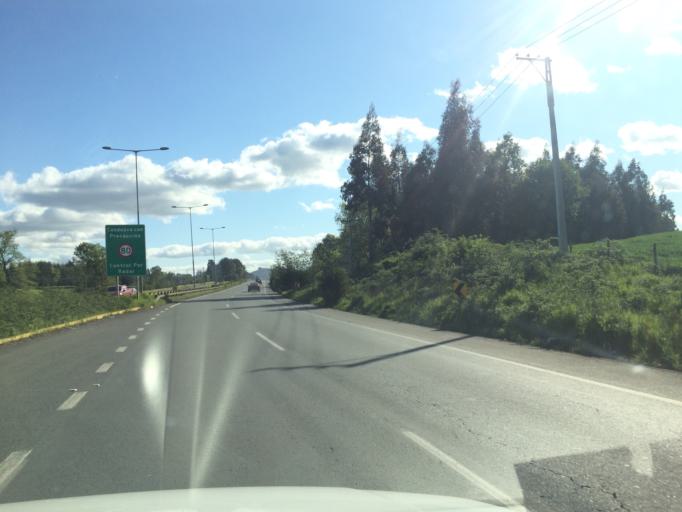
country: CL
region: Araucania
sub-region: Provincia de Cautin
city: Temuco
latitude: -38.6657
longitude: -72.4917
